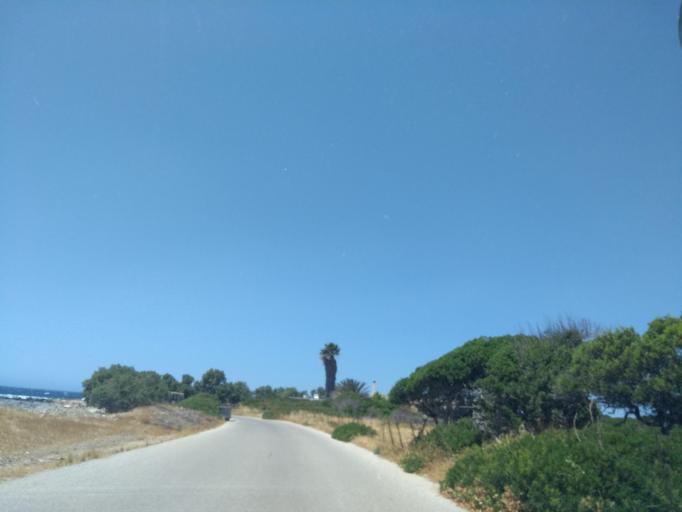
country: GR
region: Crete
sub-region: Nomos Chanias
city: Vryses
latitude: 35.3587
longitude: 23.5322
